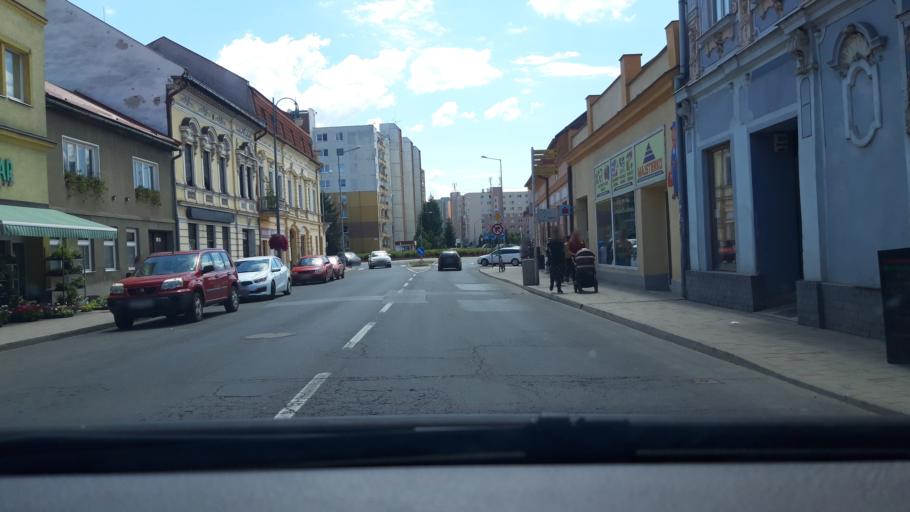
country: SK
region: Banskobystricky
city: Lucenec
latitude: 48.3268
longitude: 19.6688
